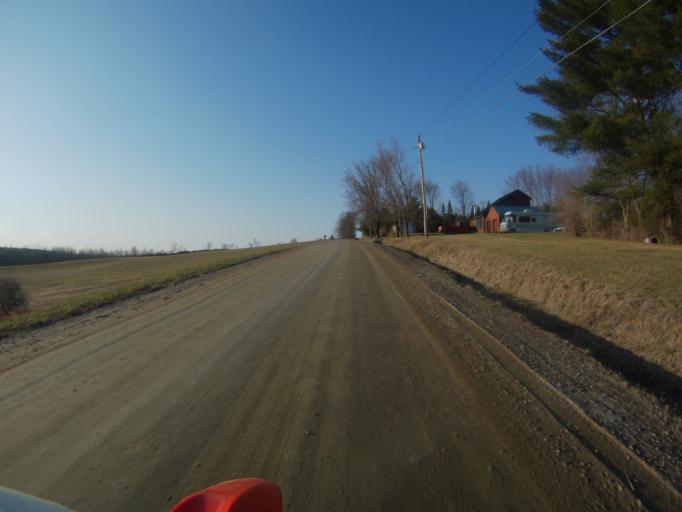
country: US
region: Vermont
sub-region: Addison County
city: Bristol
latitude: 44.1038
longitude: -73.0884
